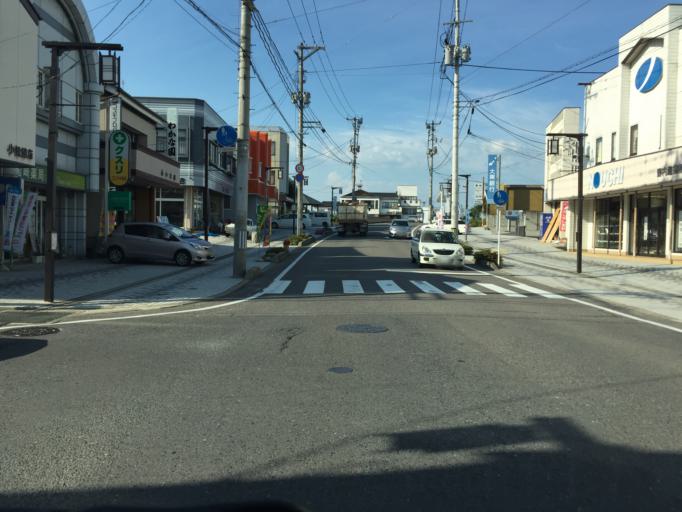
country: JP
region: Fukushima
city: Motomiya
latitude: 37.5158
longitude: 140.4033
